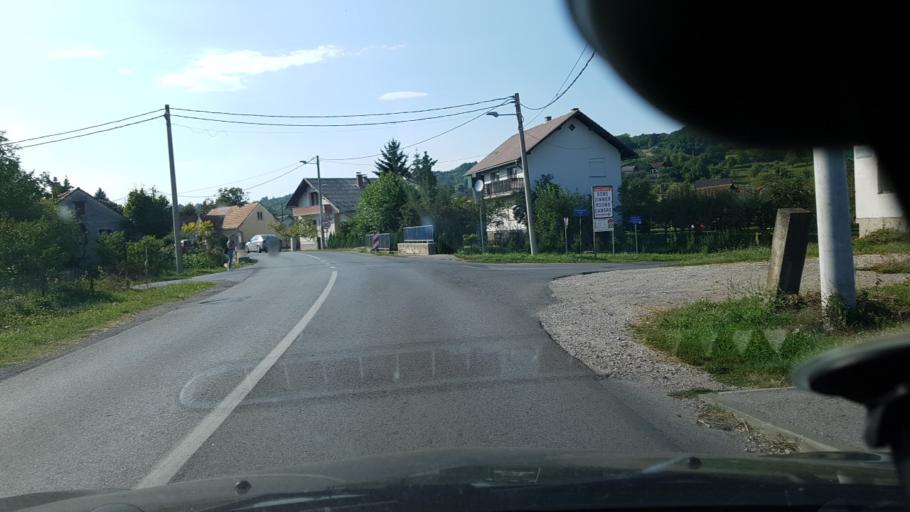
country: HR
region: Zagrebacka
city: Bregana
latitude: 45.8823
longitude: 15.7228
